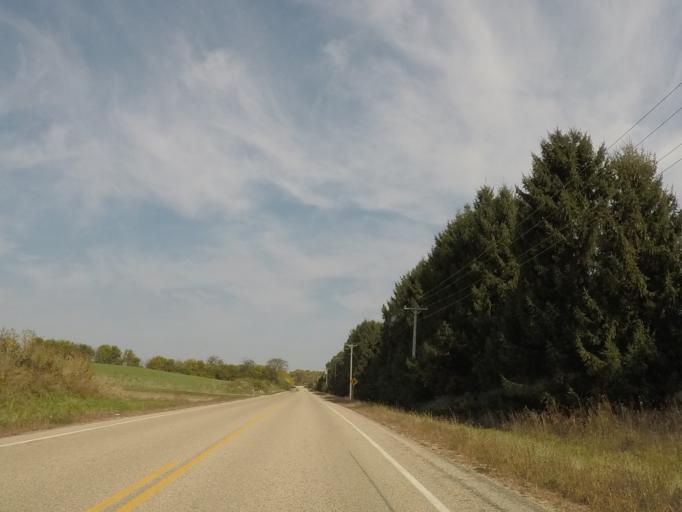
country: US
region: Wisconsin
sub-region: Dane County
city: Cross Plains
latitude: 43.0397
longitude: -89.6162
